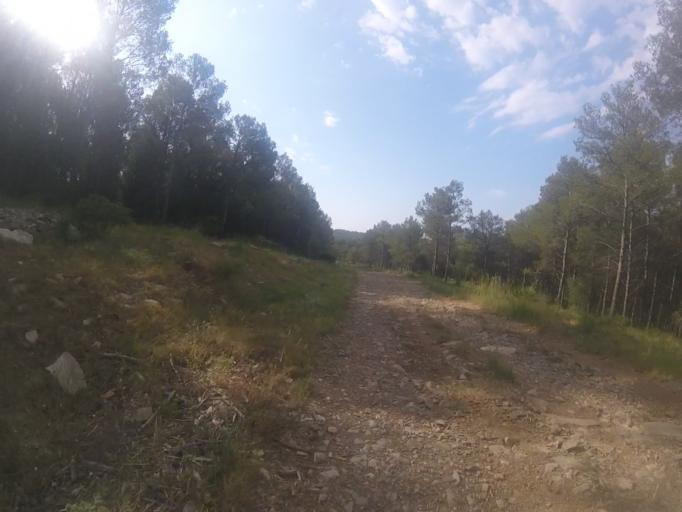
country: ES
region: Valencia
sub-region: Provincia de Castello
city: Cervera del Maestre
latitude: 40.4007
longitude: 0.2048
